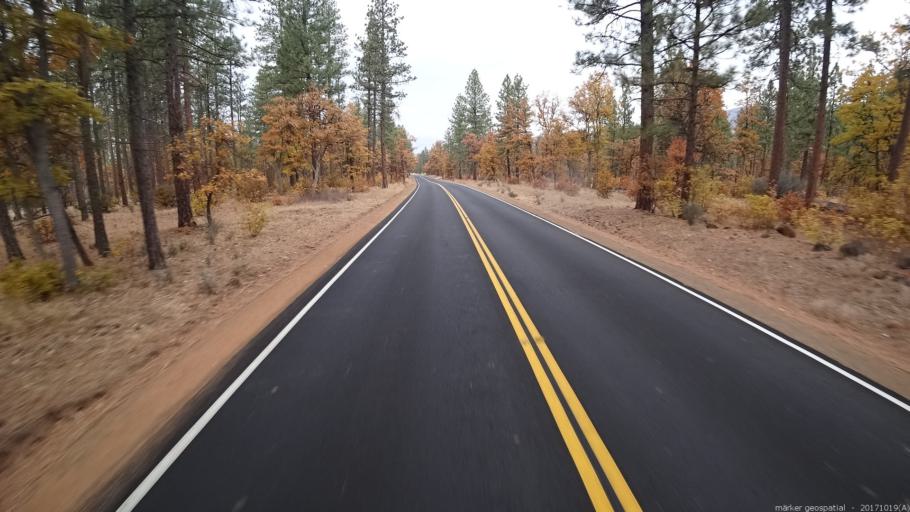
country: US
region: California
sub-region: Shasta County
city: Burney
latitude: 41.1223
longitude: -121.3327
